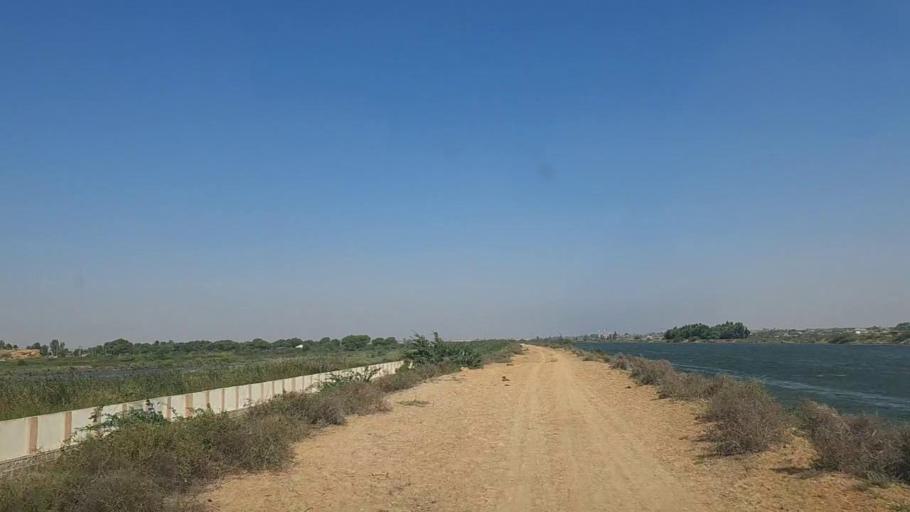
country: PK
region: Sindh
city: Thatta
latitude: 24.8149
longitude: 67.9882
